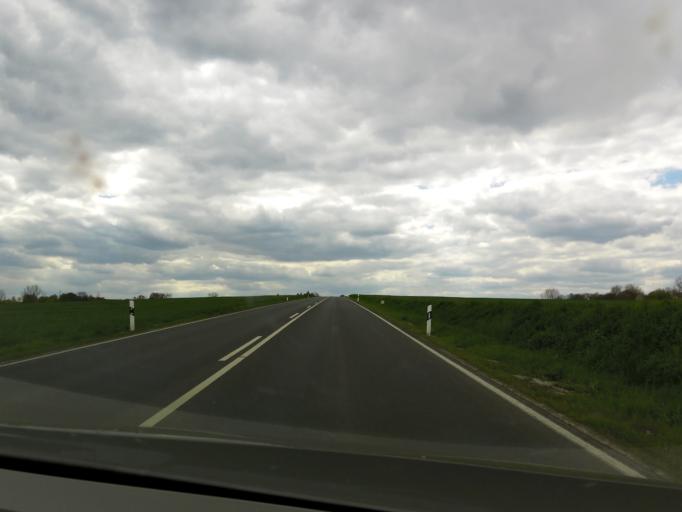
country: DE
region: Thuringia
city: Rannstedt
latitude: 51.0924
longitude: 11.5421
